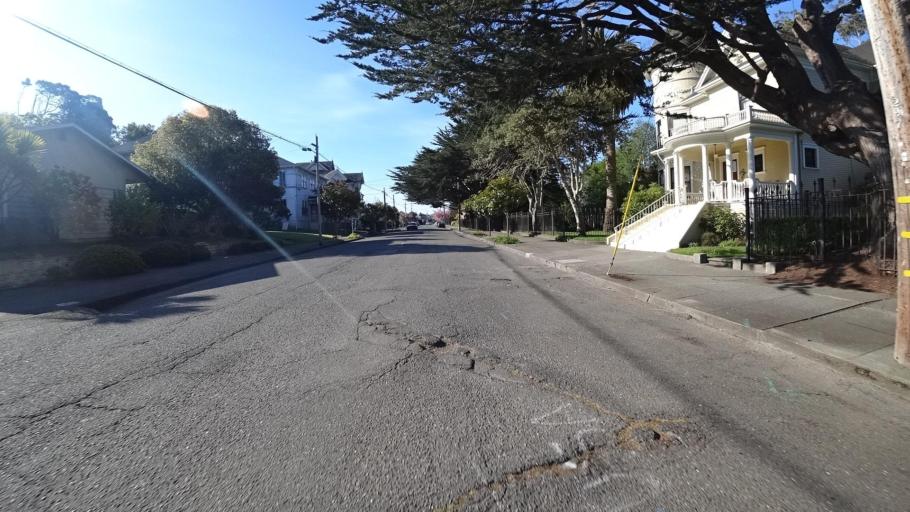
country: US
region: California
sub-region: Humboldt County
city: Eureka
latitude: 40.7931
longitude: -124.1628
